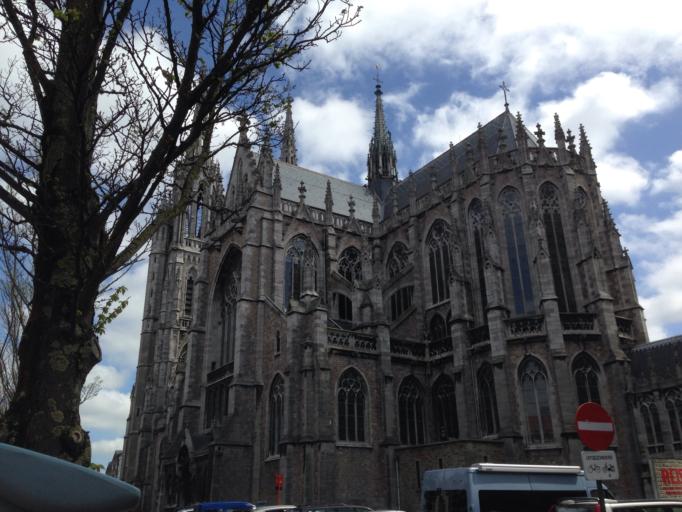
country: BE
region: Flanders
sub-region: Provincie West-Vlaanderen
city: Ostend
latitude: 51.2299
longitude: 2.9205
